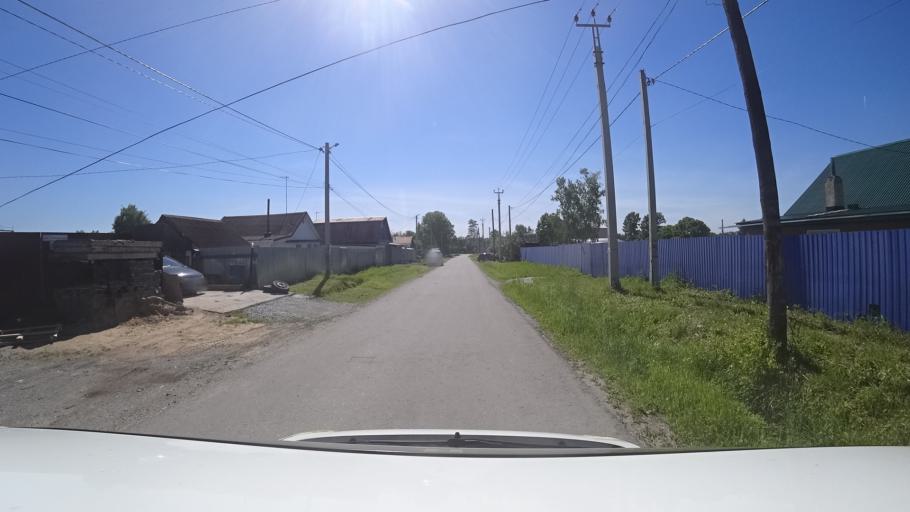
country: RU
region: Khabarovsk Krai
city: Topolevo
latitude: 48.5538
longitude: 135.1939
